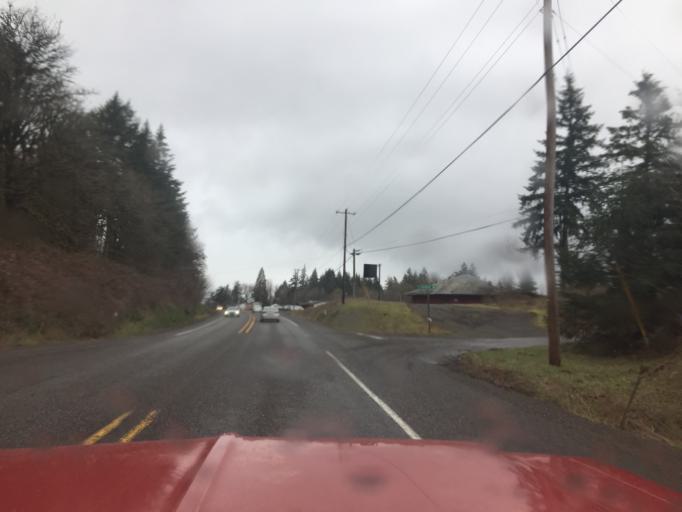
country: US
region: Oregon
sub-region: Columbia County
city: Rainier
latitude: 46.0629
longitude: -122.8957
